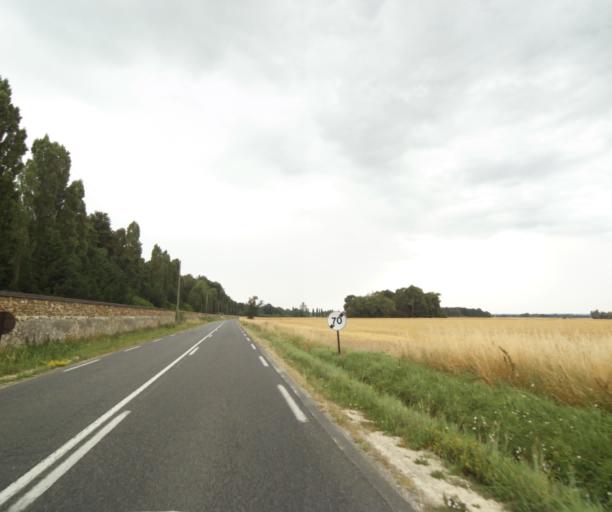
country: FR
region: Ile-de-France
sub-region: Departement de Seine-et-Marne
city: Perthes
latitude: 48.4874
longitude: 2.5723
